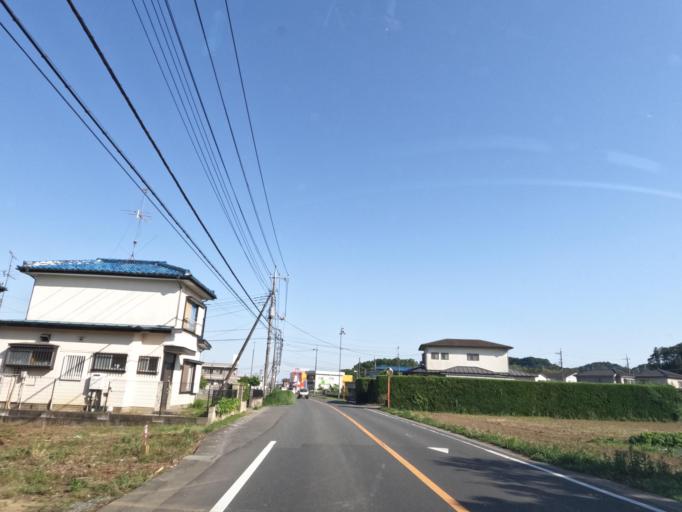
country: JP
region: Saitama
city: Ogawa
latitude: 36.0635
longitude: 139.3056
